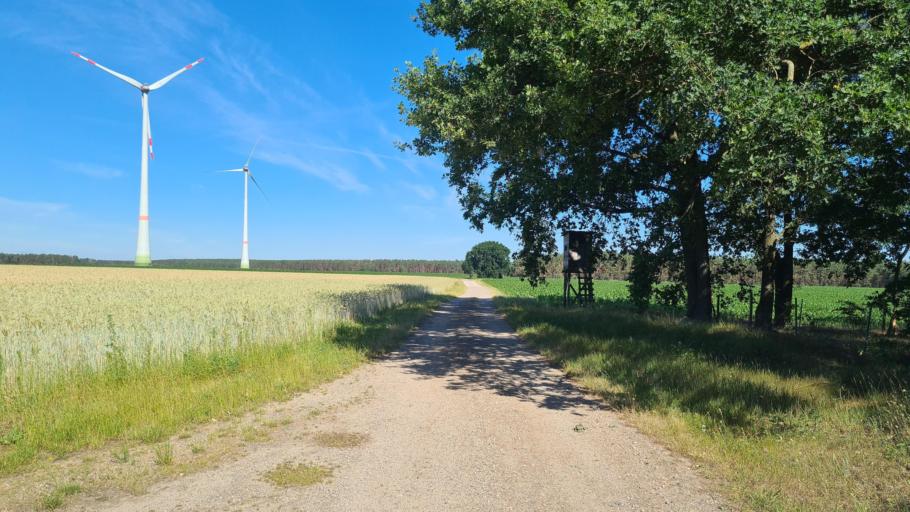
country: DE
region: Brandenburg
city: Treuenbrietzen
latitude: 52.0274
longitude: 12.8558
